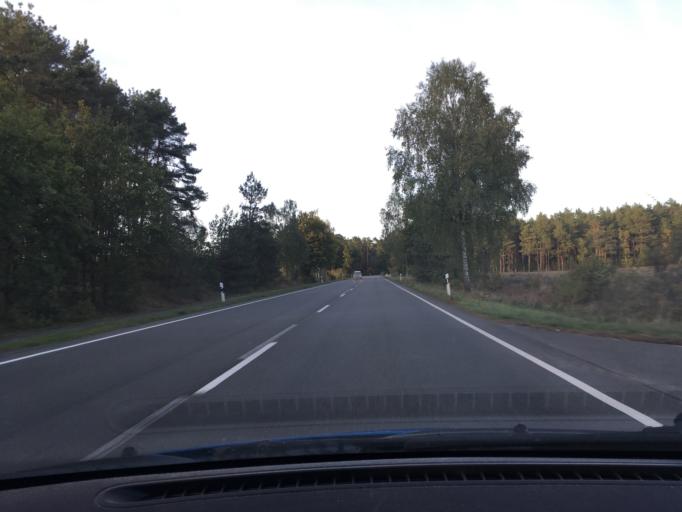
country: DE
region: Lower Saxony
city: Betzendorf
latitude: 53.1684
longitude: 10.3056
